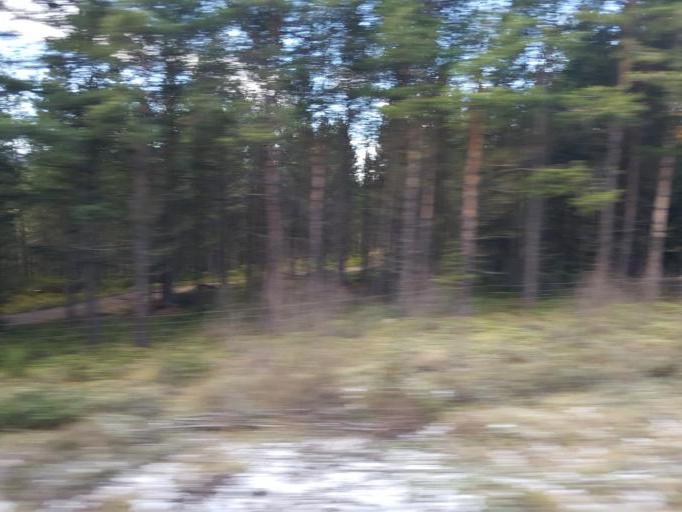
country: NO
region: Oppland
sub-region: Dovre
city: Dombas
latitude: 62.0874
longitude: 9.1416
